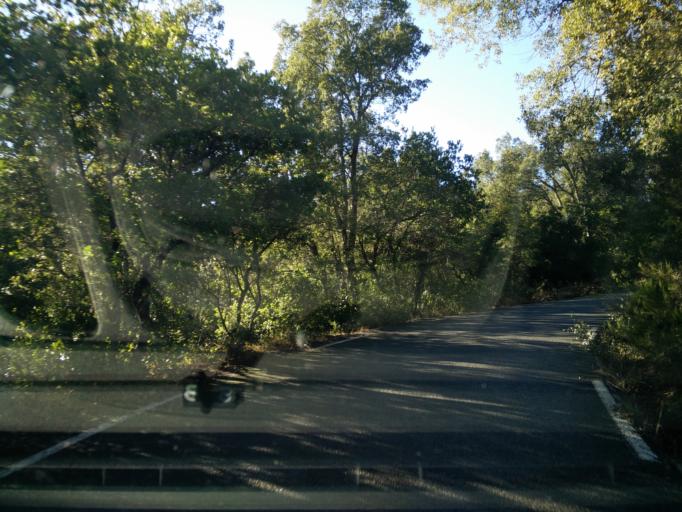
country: FR
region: Provence-Alpes-Cote d'Azur
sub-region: Departement du Var
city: Collobrieres
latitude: 43.2375
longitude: 6.3593
